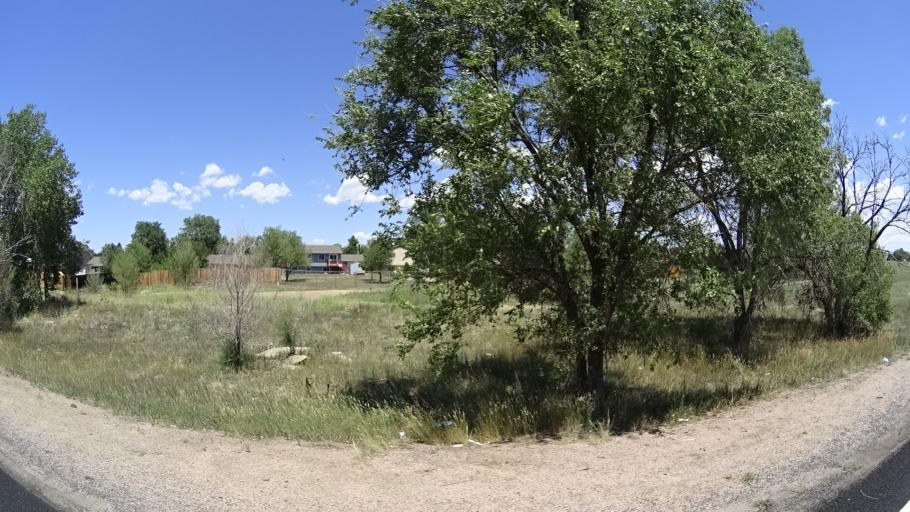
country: US
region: Colorado
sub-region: El Paso County
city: Stratmoor
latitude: 38.7887
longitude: -104.7431
